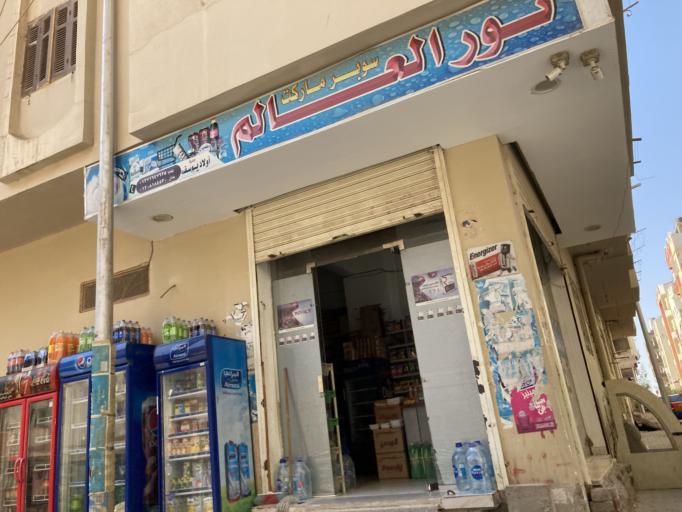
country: EG
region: Red Sea
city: Hurghada
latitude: 27.2494
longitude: 33.8330
